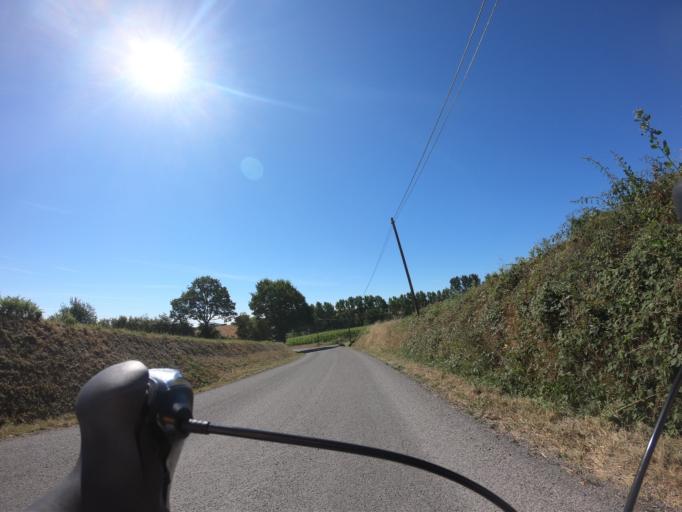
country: FR
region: Lower Normandy
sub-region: Departement de l'Orne
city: Saint-Denis-sur-Sarthon
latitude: 48.5281
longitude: -0.0931
